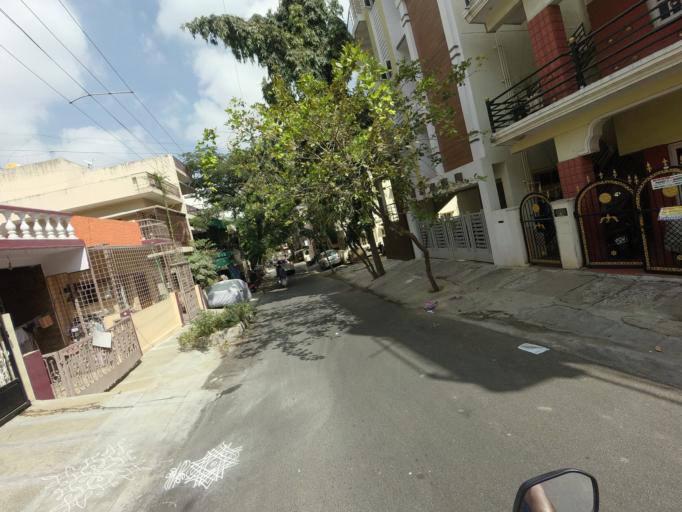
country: IN
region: Karnataka
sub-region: Bangalore Urban
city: Bangalore
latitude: 12.9580
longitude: 77.5361
